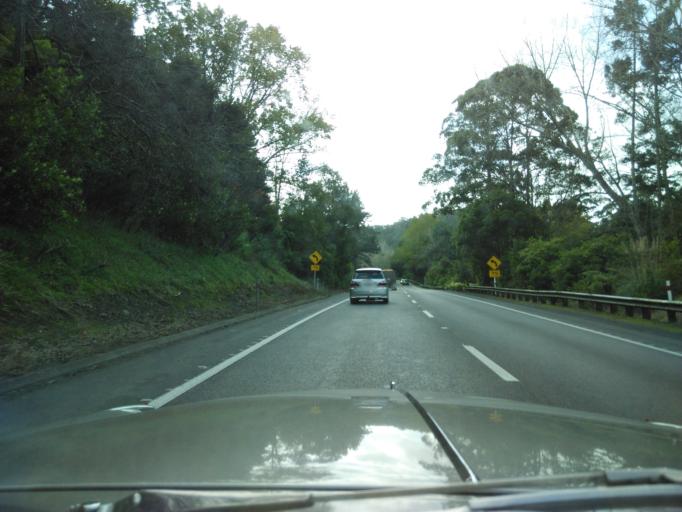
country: NZ
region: Auckland
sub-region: Auckland
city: Warkworth
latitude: -36.4457
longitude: 174.6500
